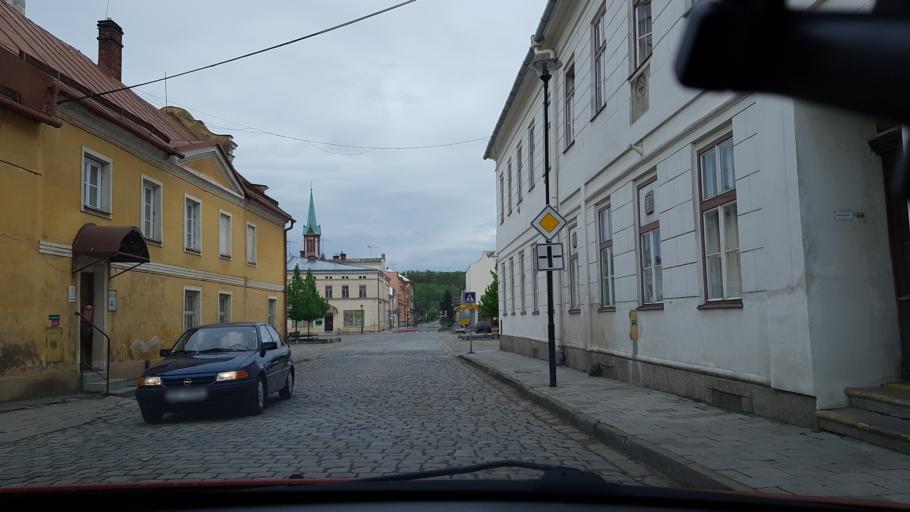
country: CZ
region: Olomoucky
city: Vidnava
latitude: 50.3729
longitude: 17.1852
